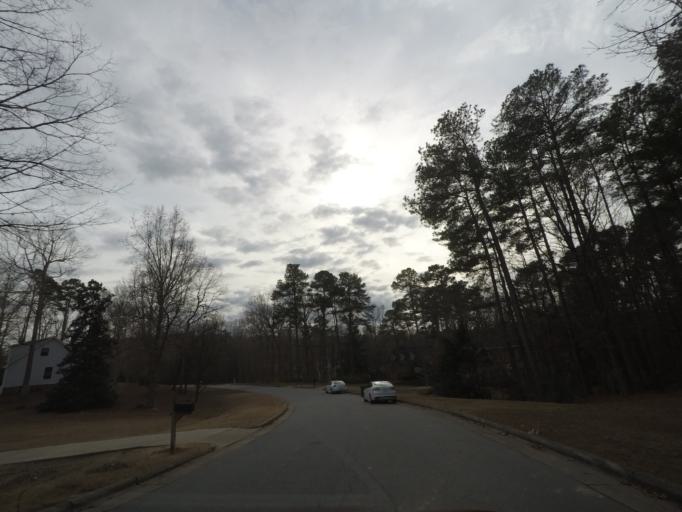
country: US
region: North Carolina
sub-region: Durham County
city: Durham
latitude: 36.0441
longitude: -78.9595
